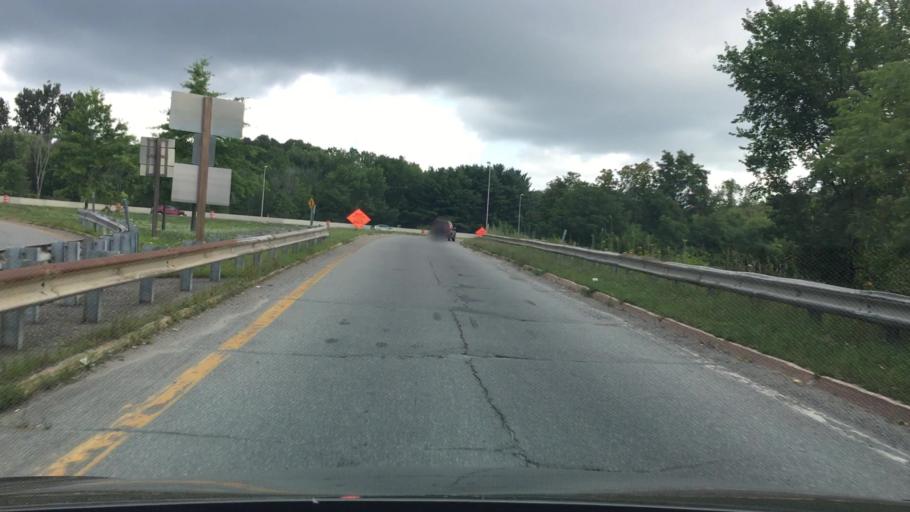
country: US
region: Maine
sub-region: Penobscot County
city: Bangor
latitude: 44.8182
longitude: -68.7731
